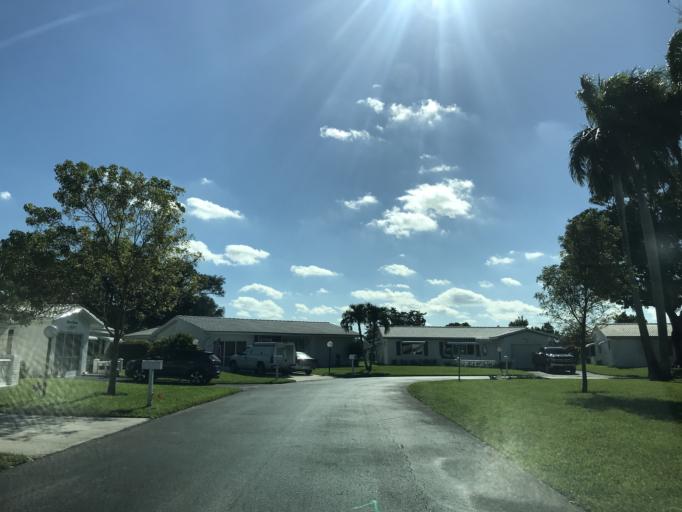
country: US
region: Florida
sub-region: Broward County
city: Plantation
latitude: 26.1428
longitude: -80.2609
